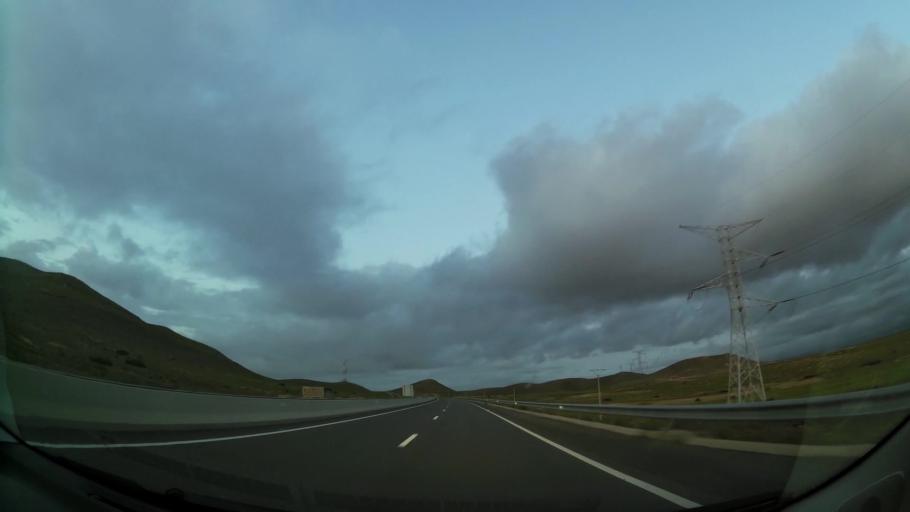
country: MA
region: Oriental
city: El Aioun
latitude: 34.6141
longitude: -2.4258
